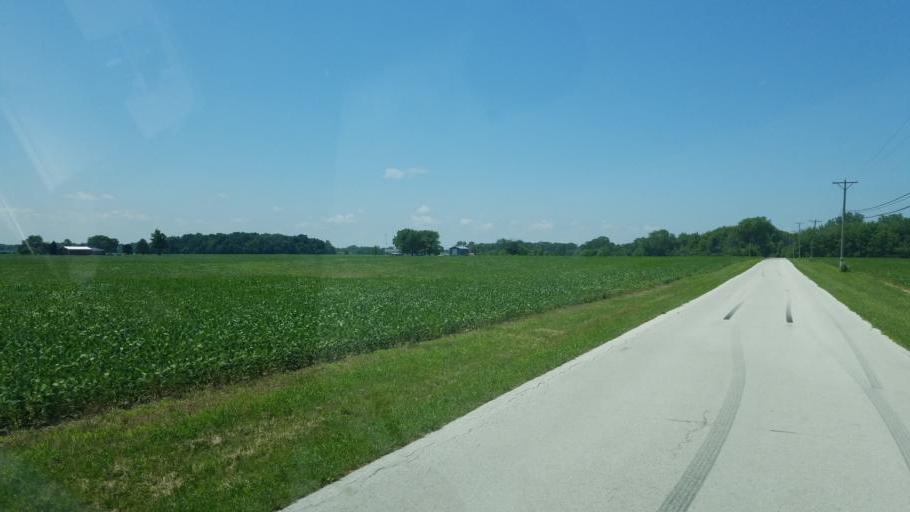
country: US
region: Ohio
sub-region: Sandusky County
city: Fremont
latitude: 41.4033
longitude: -83.0729
